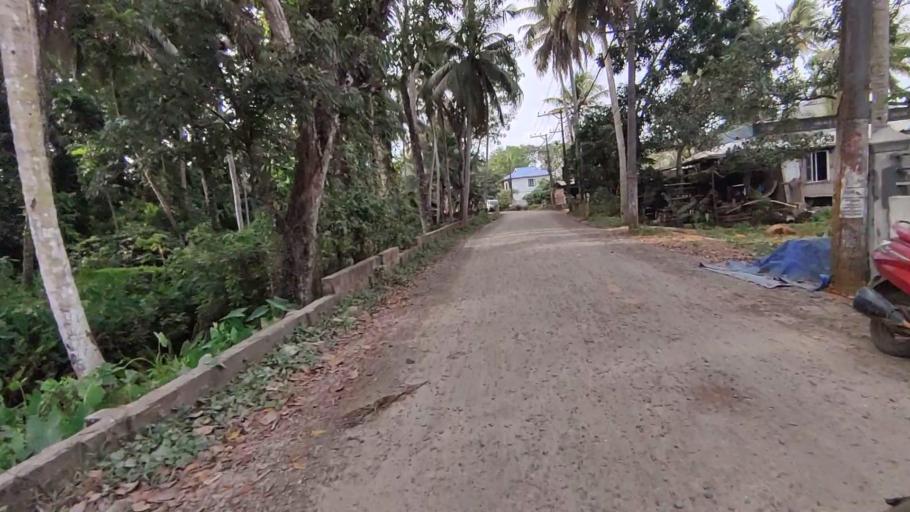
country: IN
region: Kerala
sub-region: Kottayam
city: Kottayam
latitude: 9.5806
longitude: 76.4917
